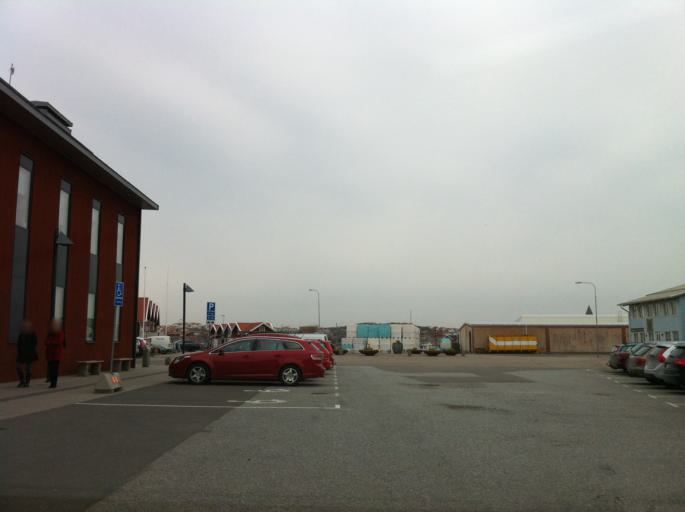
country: SE
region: Vaestra Goetaland
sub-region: Tjorns Kommun
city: Myggenas
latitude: 58.1445
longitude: 11.7089
